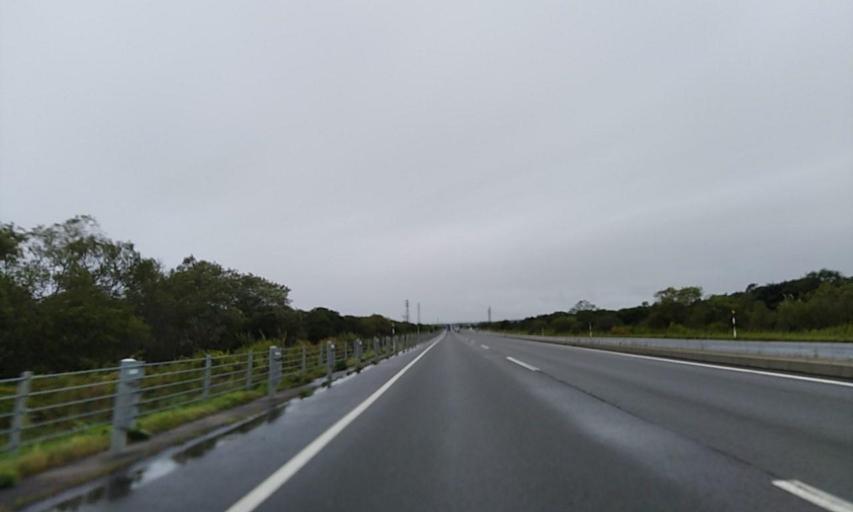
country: JP
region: Hokkaido
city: Kushiro
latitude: 43.0316
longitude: 144.3054
